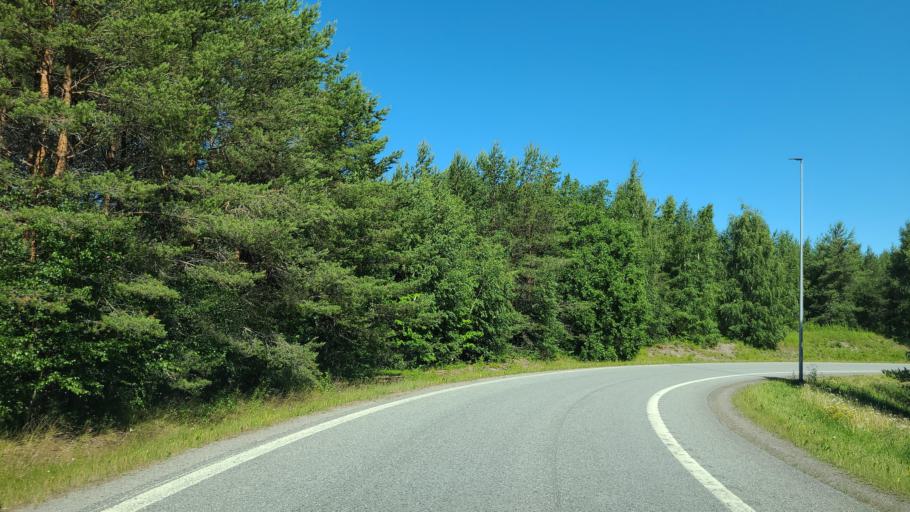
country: FI
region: Ostrobothnia
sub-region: Vaasa
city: Ristinummi
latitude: 63.0549
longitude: 21.7103
